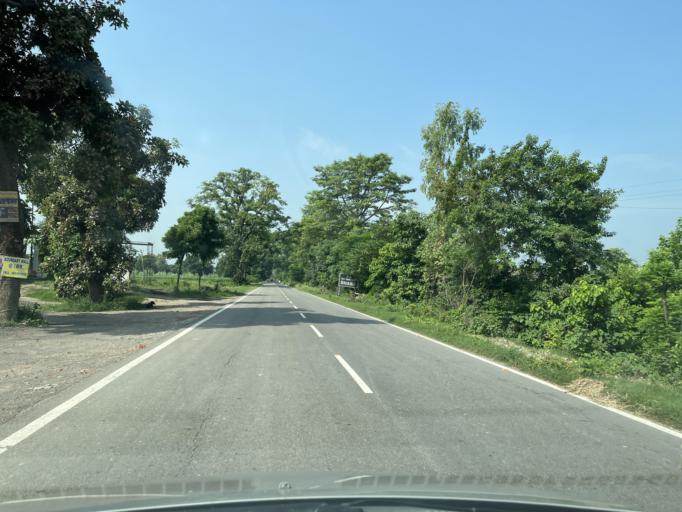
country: IN
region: Uttarakhand
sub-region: Udham Singh Nagar
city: Bazpur
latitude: 29.1924
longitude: 79.1933
